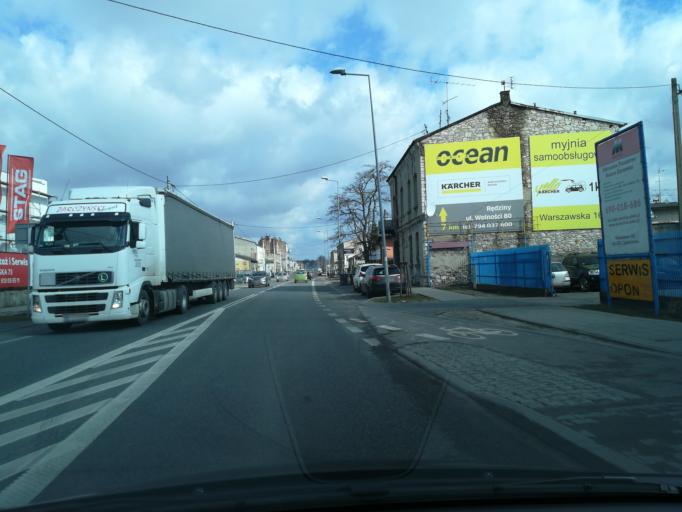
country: PL
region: Silesian Voivodeship
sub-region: Czestochowa
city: Czestochowa
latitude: 50.8193
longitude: 19.1306
